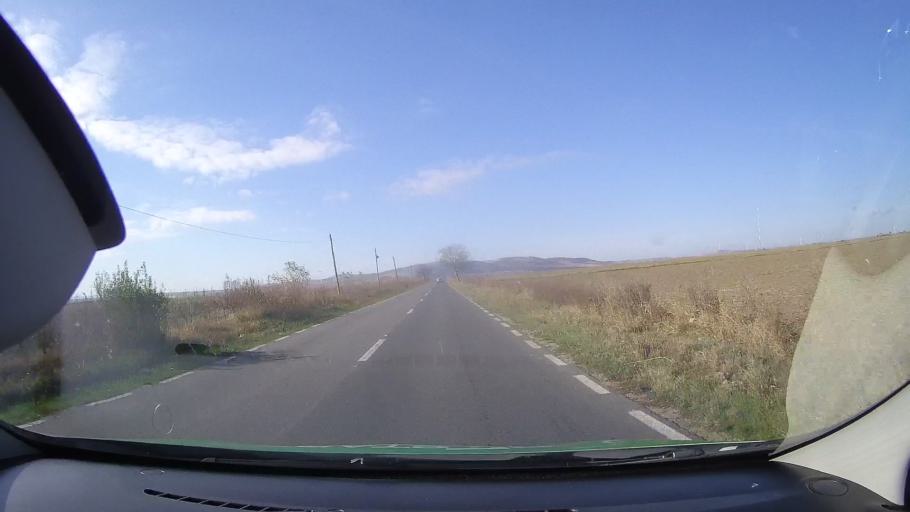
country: RO
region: Tulcea
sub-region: Comuna Valea Nucarilor
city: Valea Nucarilor
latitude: 45.0382
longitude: 28.9105
